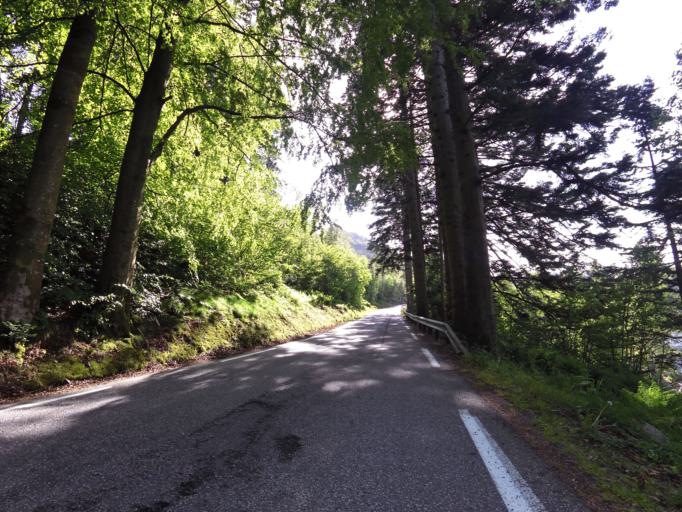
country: NO
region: Rogaland
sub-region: Sokndal
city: Hauge i Dalane
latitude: 58.3151
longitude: 6.3472
